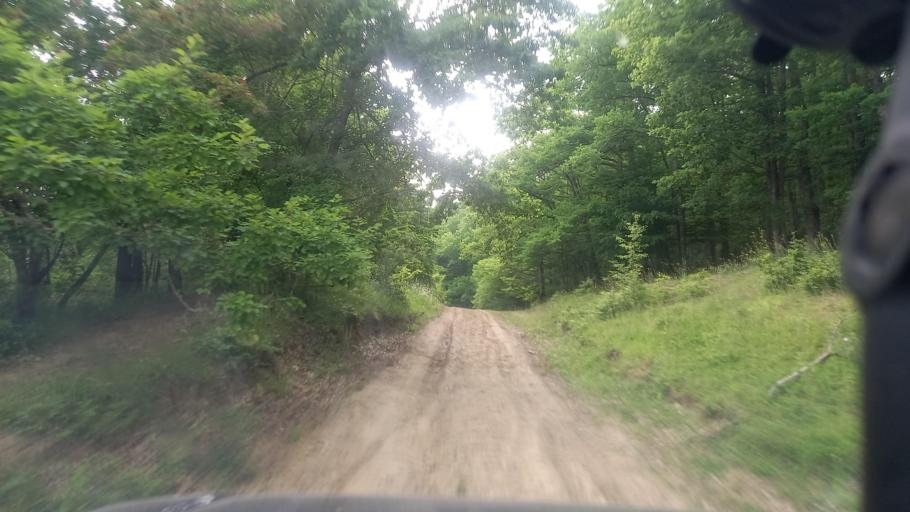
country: RU
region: Krasnodarskiy
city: Goryachiy Klyuch
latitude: 44.6058
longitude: 38.9900
